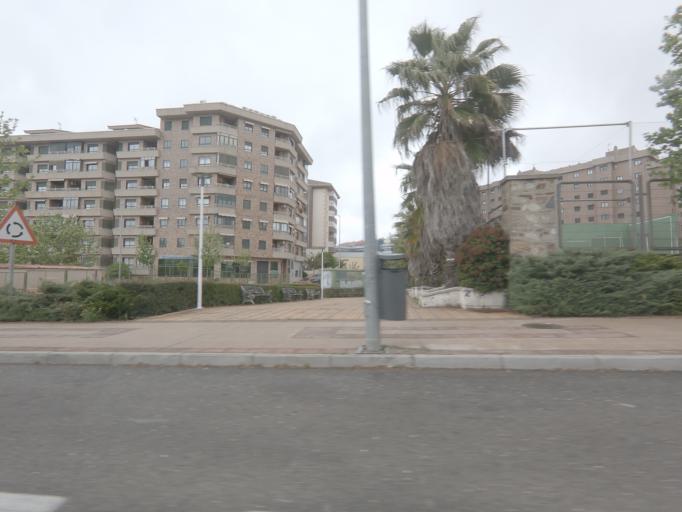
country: ES
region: Extremadura
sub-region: Provincia de Caceres
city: Caceres
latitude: 39.4705
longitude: -6.3905
